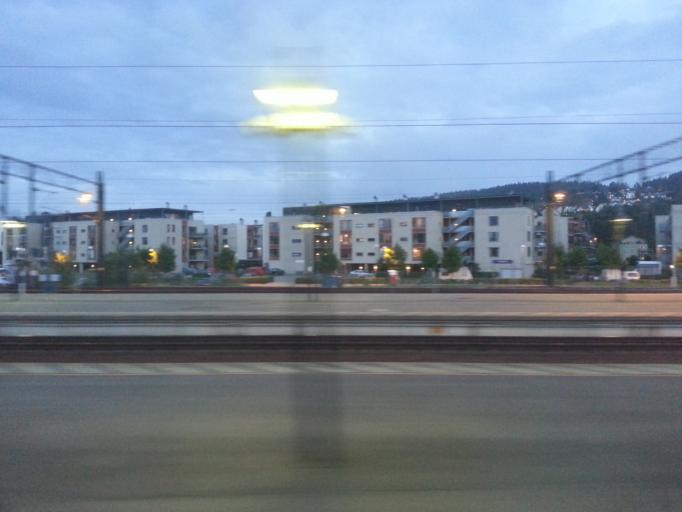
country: NO
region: Akershus
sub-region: Skedsmo
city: Lillestrom
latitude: 59.9526
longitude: 11.0421
